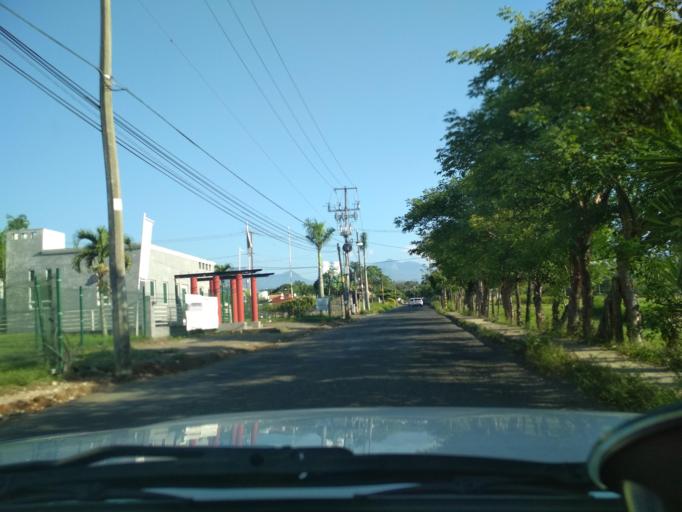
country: MX
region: Veracruz
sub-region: Fortin
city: Fraccionamiento Villas de la Llave
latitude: 18.9144
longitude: -96.9880
